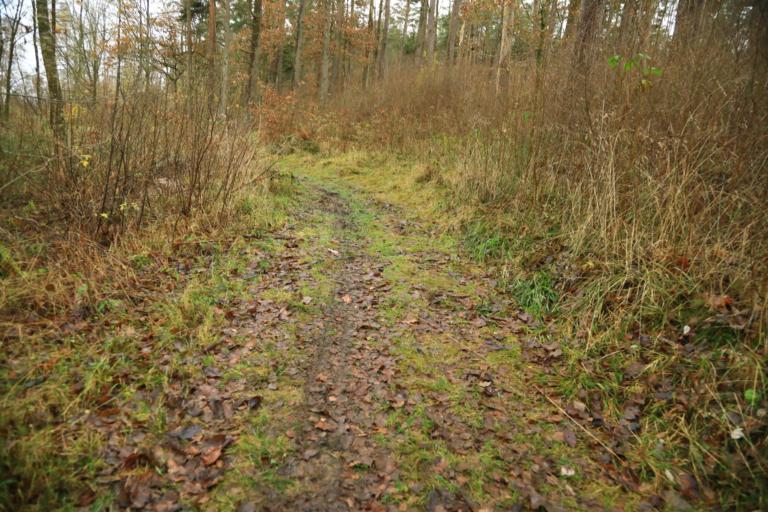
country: SE
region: Halland
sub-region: Varbergs Kommun
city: Varberg
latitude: 57.1752
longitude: 12.2125
